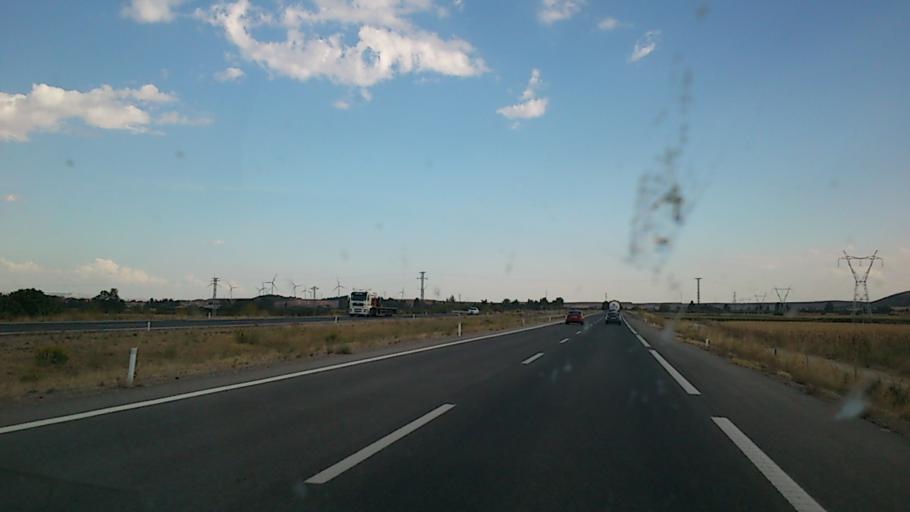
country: ES
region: Aragon
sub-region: Provincia de Zaragoza
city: Frescano
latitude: 41.9025
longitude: -1.4462
